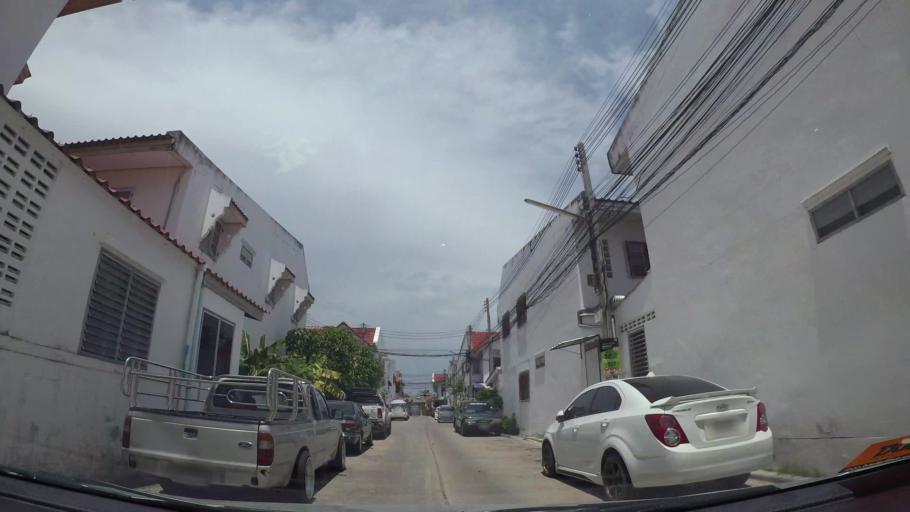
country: TH
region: Chon Buri
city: Chon Buri
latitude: 13.3315
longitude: 100.9421
